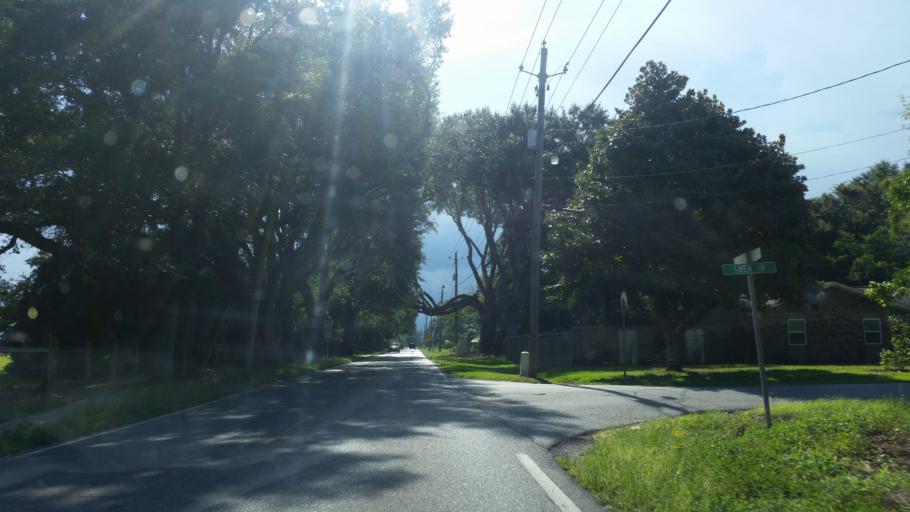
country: US
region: Florida
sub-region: Santa Rosa County
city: Pace
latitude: 30.6324
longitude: -87.1379
